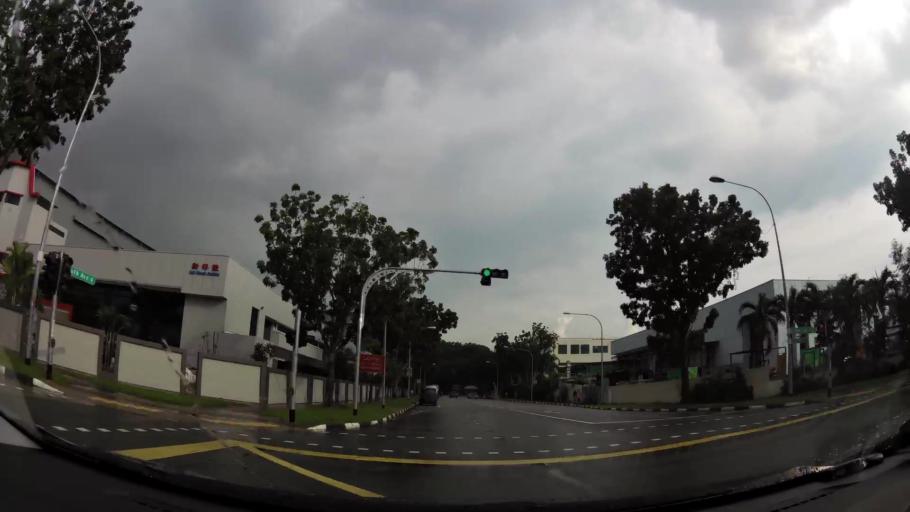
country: SG
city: Singapore
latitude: 1.3357
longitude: 103.9699
